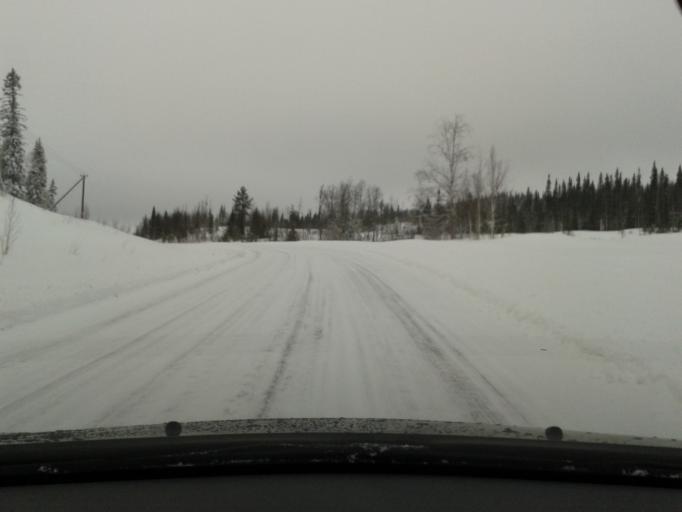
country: SE
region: Vaesterbotten
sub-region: Vilhelmina Kommun
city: Sjoberg
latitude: 65.1832
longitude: 15.9166
